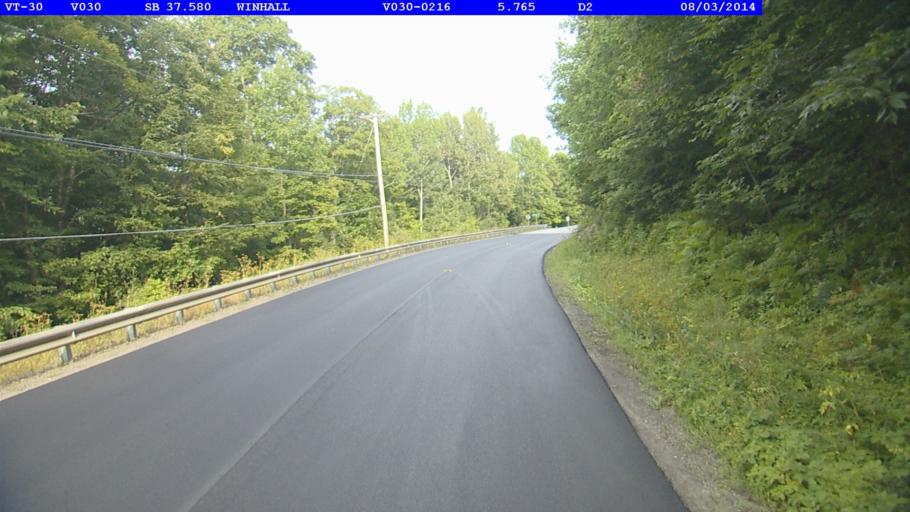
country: US
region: Vermont
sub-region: Bennington County
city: Manchester Center
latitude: 43.1889
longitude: -72.9384
